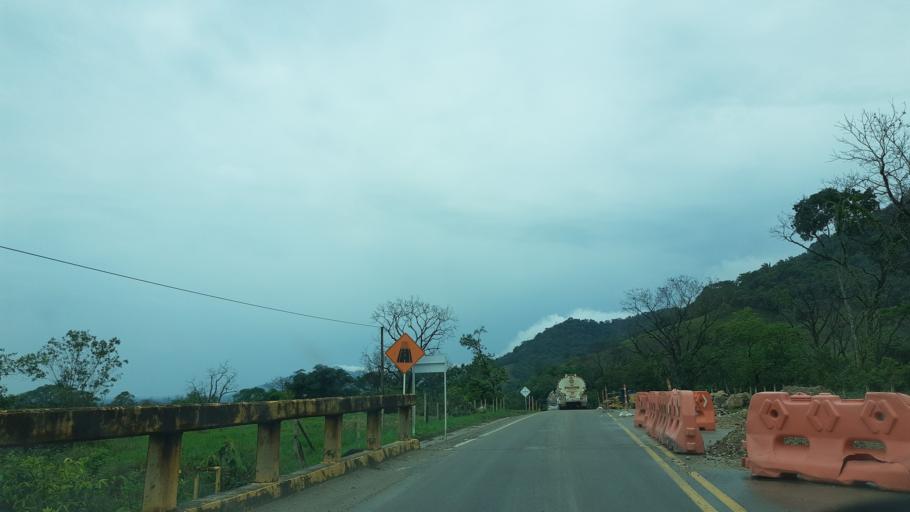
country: CO
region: Casanare
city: Sabanalarga
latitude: 4.8228
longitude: -72.9671
